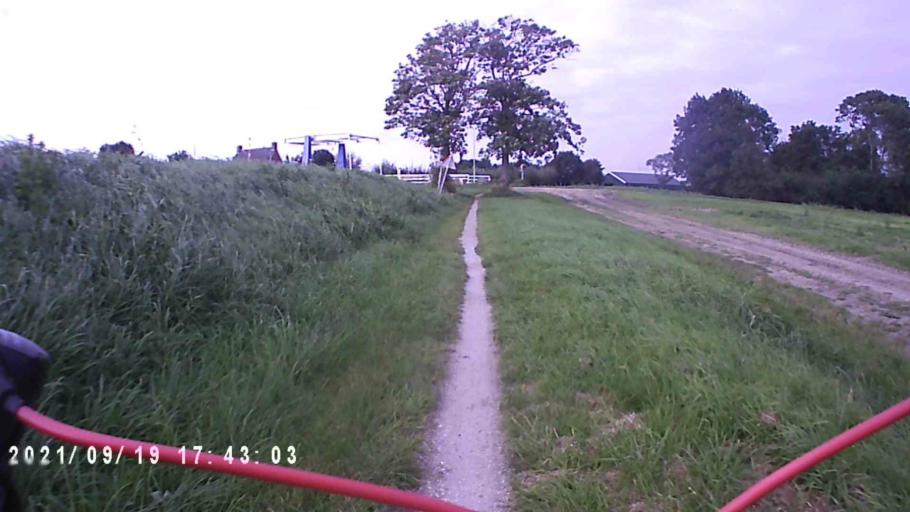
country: NL
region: Groningen
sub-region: Gemeente Delfzijl
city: Delfzijl
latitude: 53.2597
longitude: 6.9690
